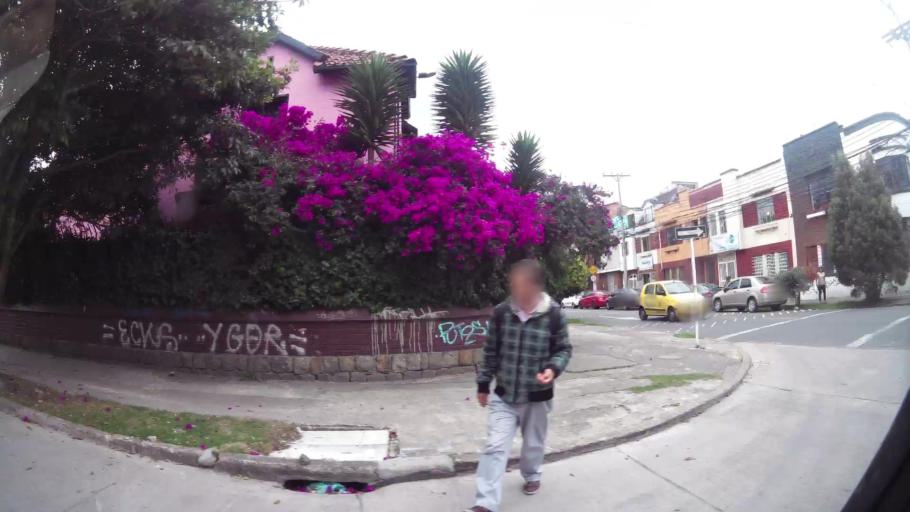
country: CO
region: Bogota D.C.
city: Bogota
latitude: 4.6190
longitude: -74.0729
